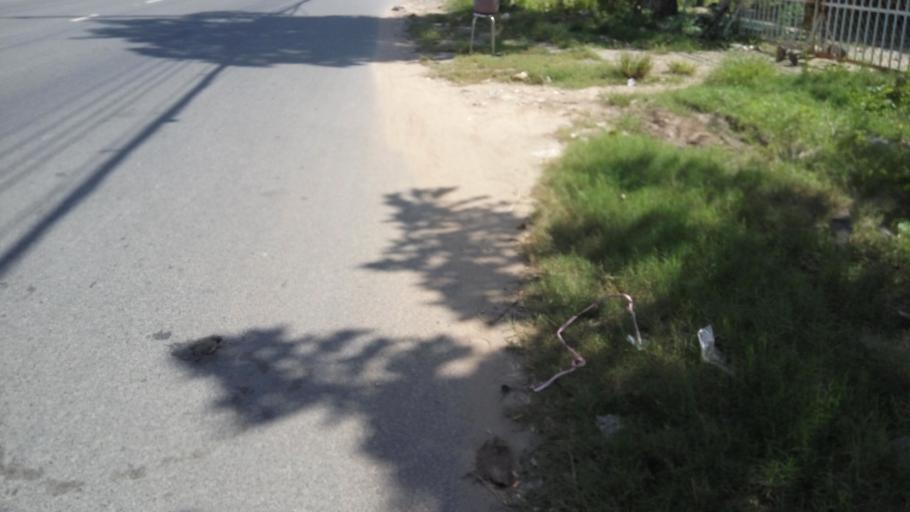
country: VN
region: An Giang
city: An Chau
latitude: 10.4307
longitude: 105.4006
